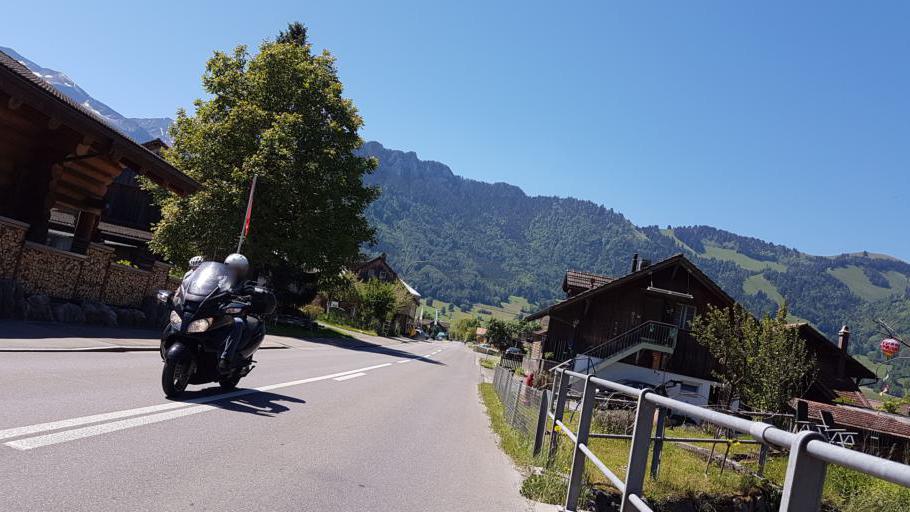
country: CH
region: Bern
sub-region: Frutigen-Niedersimmental District
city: Wimmis
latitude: 46.7051
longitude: 7.6308
